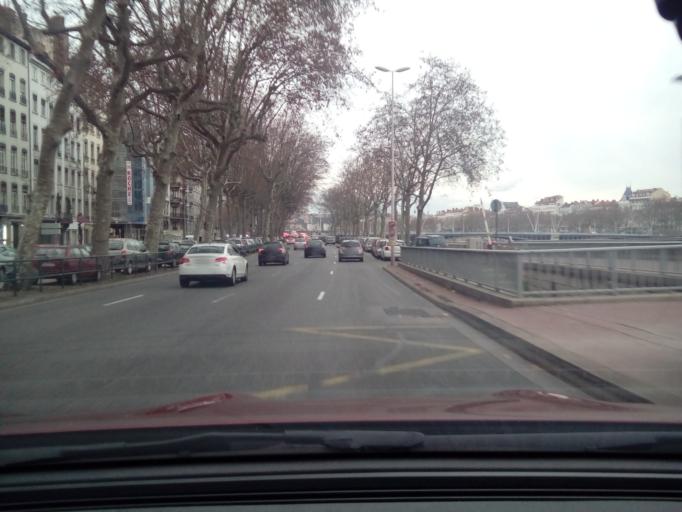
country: FR
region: Rhone-Alpes
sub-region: Departement du Rhone
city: Lyon
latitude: 45.7606
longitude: 4.8381
